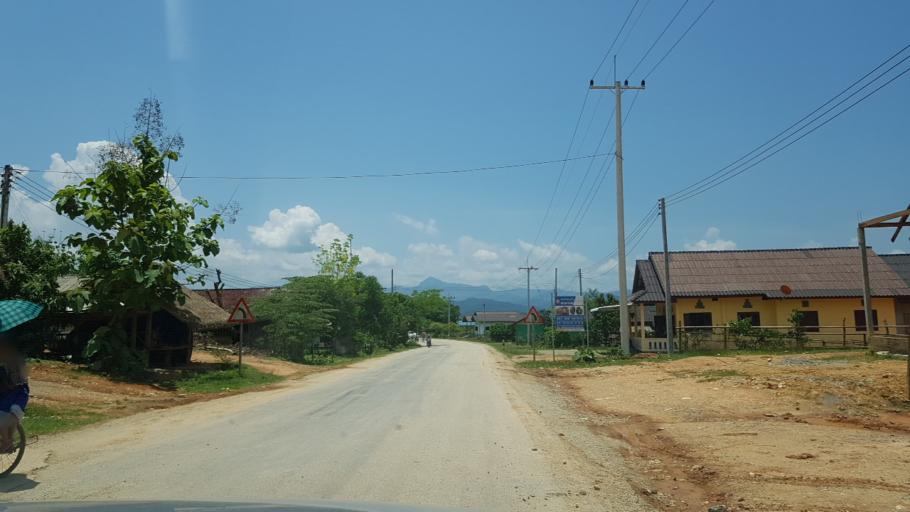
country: LA
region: Vientiane
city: Muang Kasi
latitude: 19.2646
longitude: 102.2313
